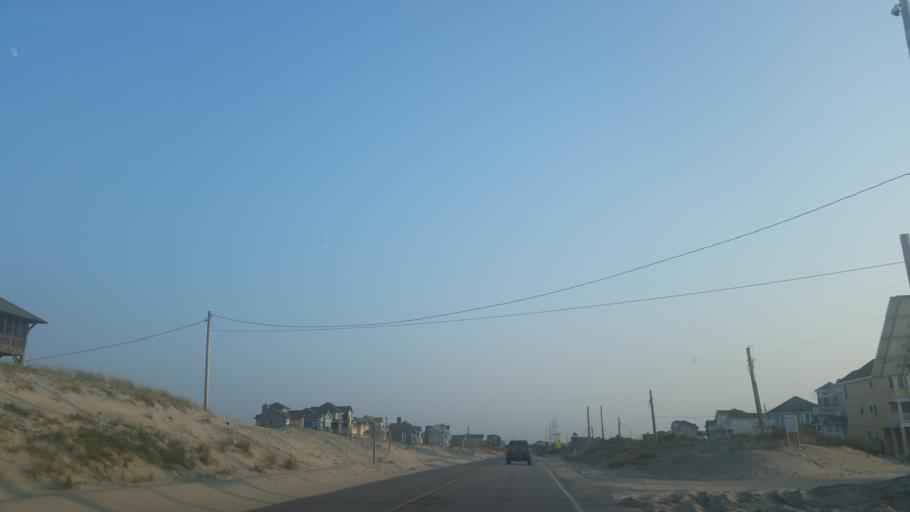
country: US
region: North Carolina
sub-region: Dare County
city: Wanchese
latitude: 35.6068
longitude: -75.4656
